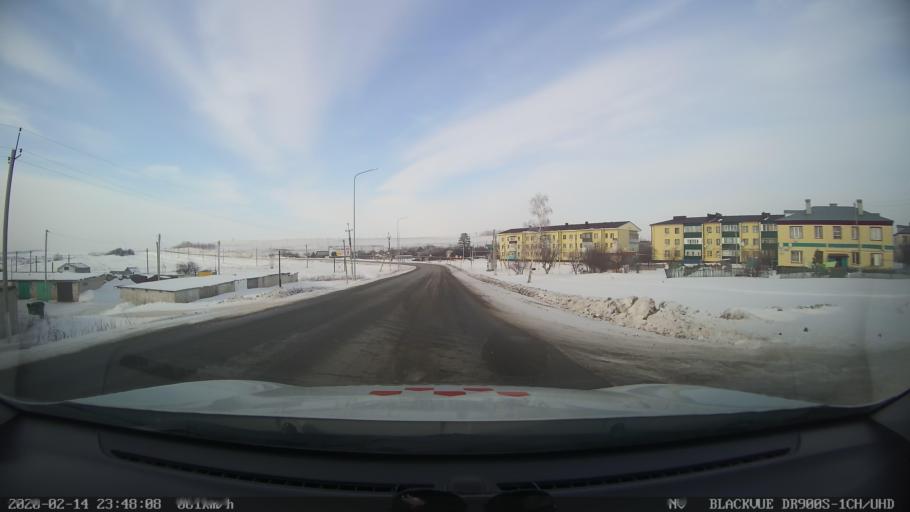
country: RU
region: Tatarstan
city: Kuybyshevskiy Zaton
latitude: 55.2458
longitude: 49.2058
